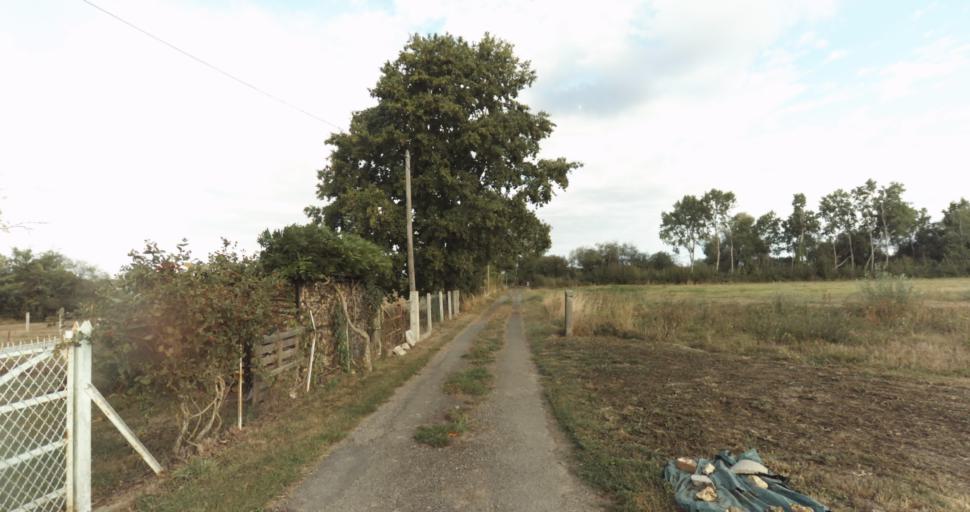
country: FR
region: Lower Normandy
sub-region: Departement de l'Orne
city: Vimoutiers
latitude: 48.9414
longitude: 0.2415
